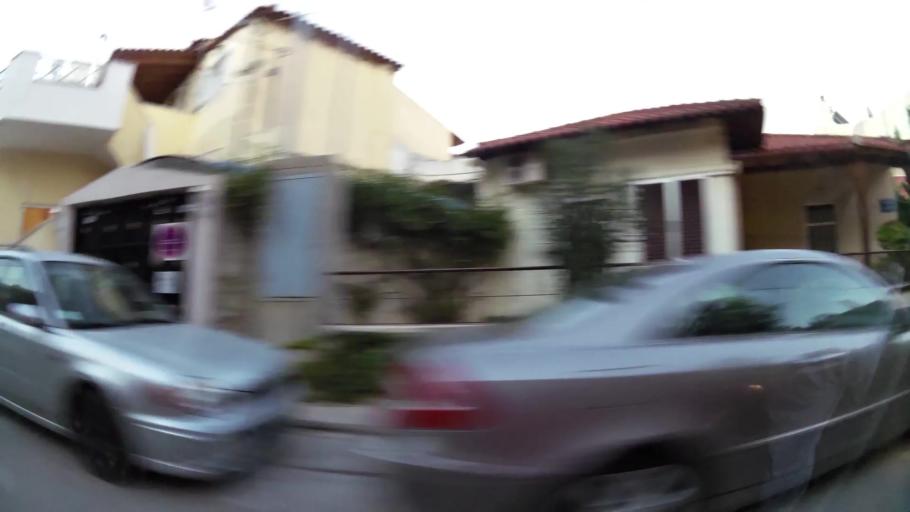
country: GR
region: Attica
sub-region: Nomarchia Anatolikis Attikis
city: Paiania
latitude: 37.9485
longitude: 23.8564
